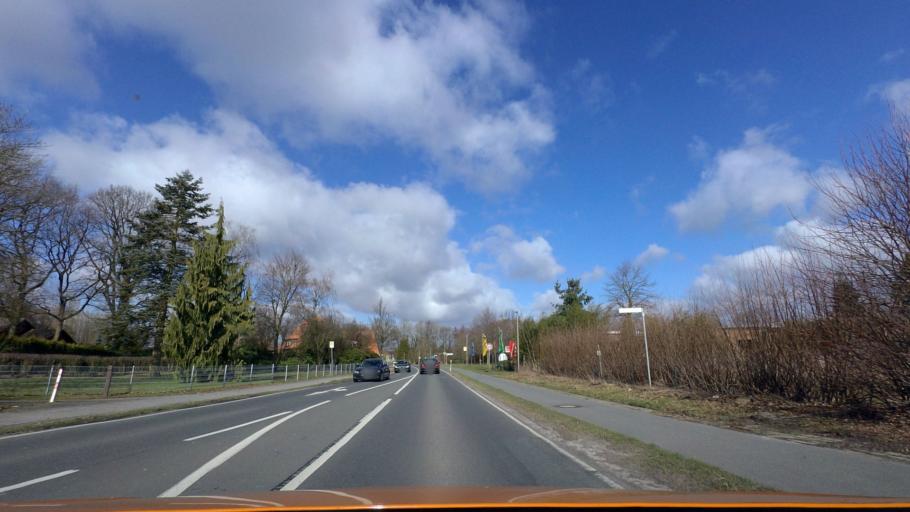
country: DE
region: Lower Saxony
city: Bad Zwischenahn
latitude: 53.1707
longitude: 7.9990
